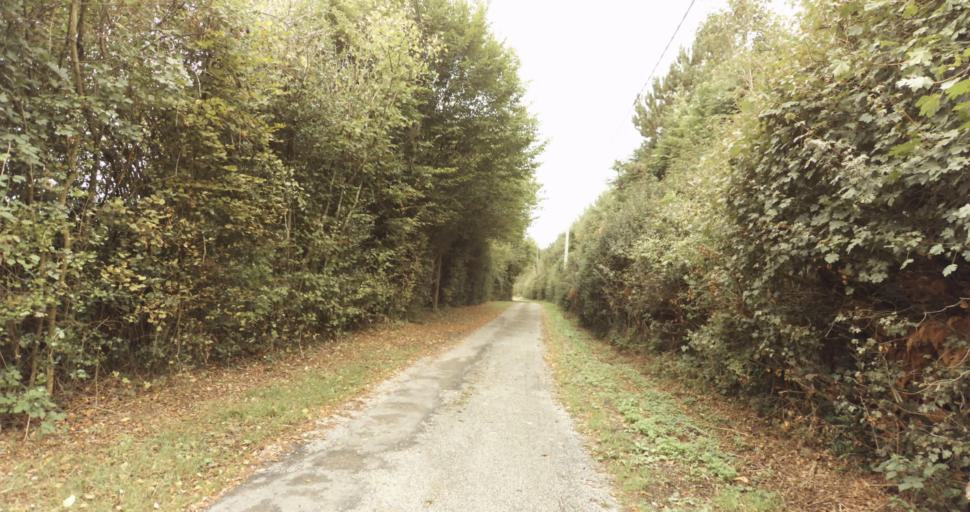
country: FR
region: Lower Normandy
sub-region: Departement de l'Orne
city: Sainte-Gauburge-Sainte-Colombe
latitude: 48.7089
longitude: 0.4555
